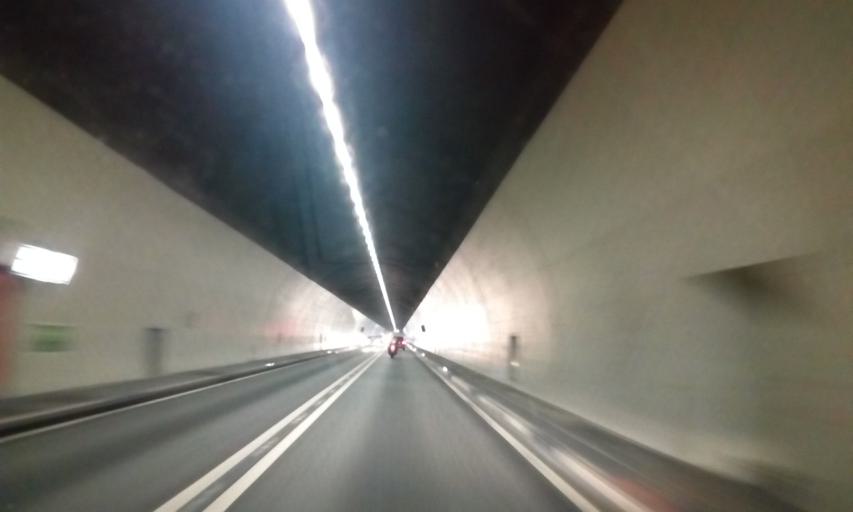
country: CH
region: Grisons
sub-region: Imboden District
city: Bonaduz
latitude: 46.8307
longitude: 9.3541
